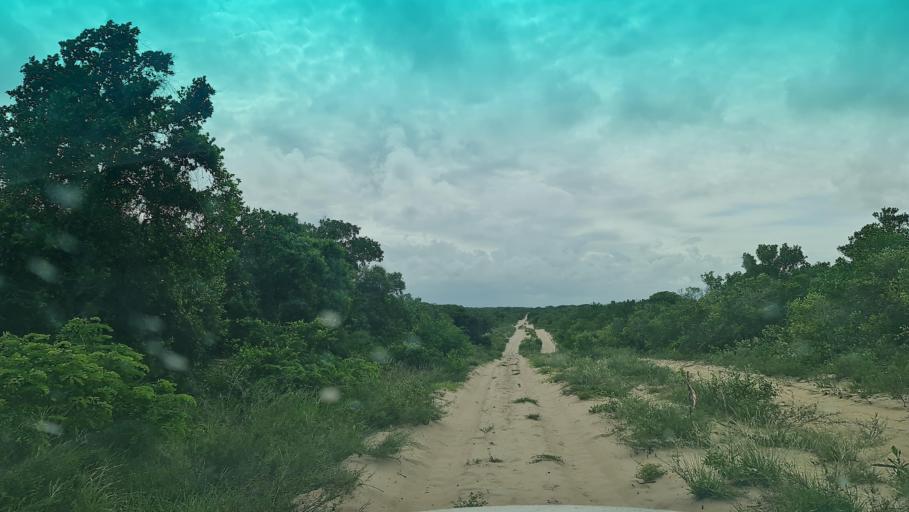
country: MZ
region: Maputo
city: Manhica
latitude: -25.4394
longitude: 32.9255
